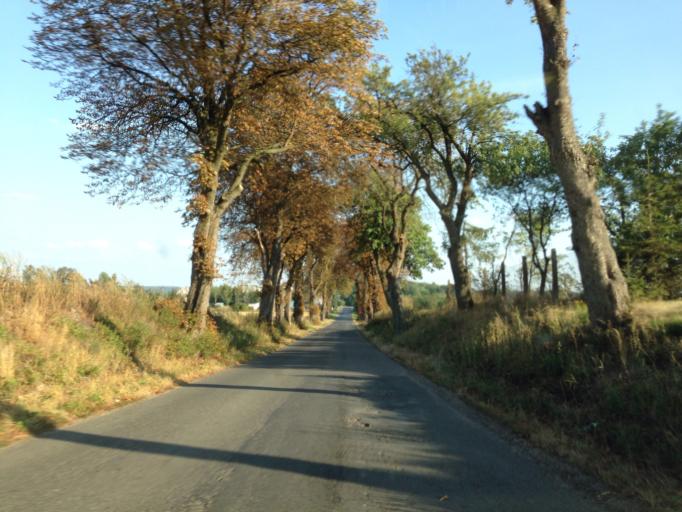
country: PL
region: Kujawsko-Pomorskie
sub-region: Powiat brodnicki
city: Brodnica
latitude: 53.2910
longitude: 19.4132
